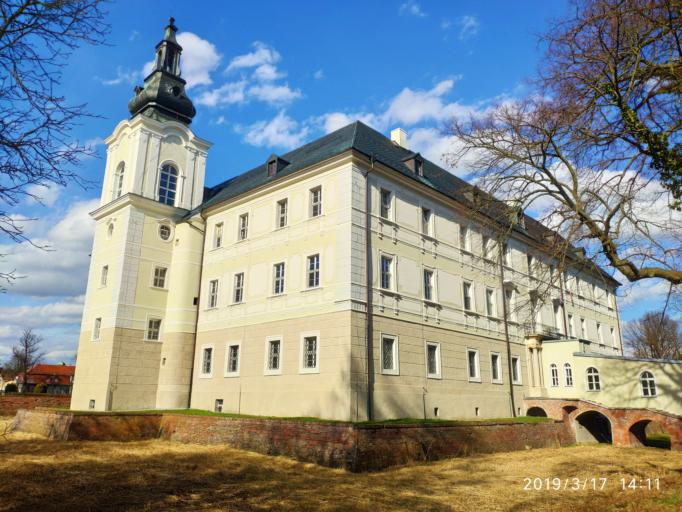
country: PL
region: Lubusz
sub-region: Powiat zielonogorski
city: Zabor
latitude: 51.9478
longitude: 15.7172
